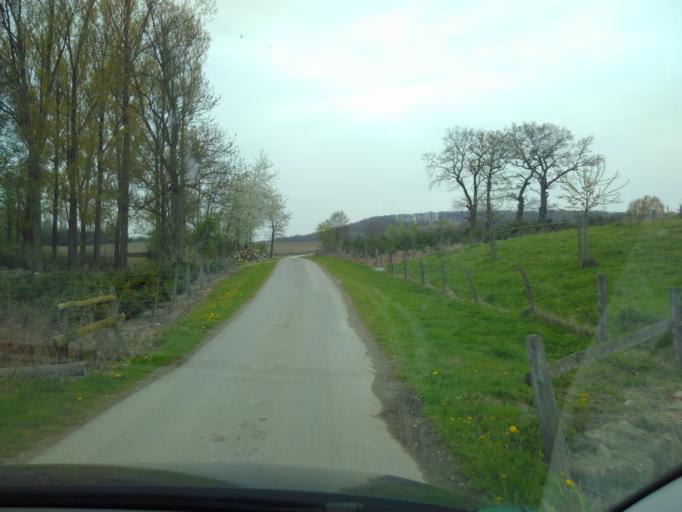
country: DE
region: North Rhine-Westphalia
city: Oelde
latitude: 51.7627
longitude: 8.1237
